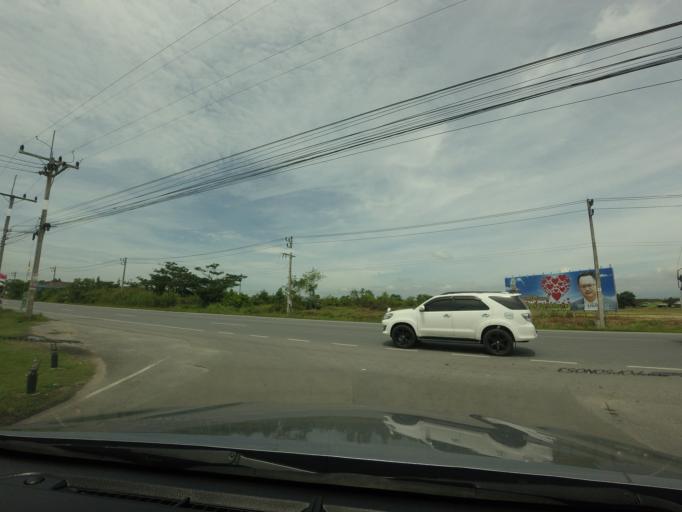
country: TH
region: Nakhon Si Thammarat
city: Nakhon Si Thammarat
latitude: 8.4386
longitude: 99.9835
